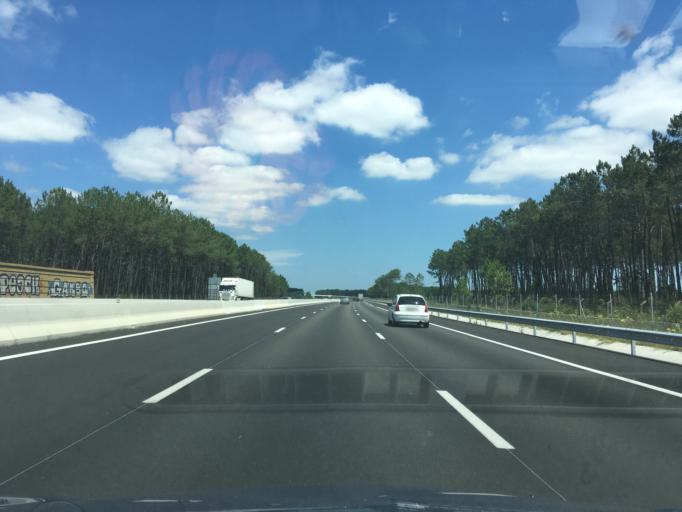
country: FR
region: Aquitaine
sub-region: Departement des Landes
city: Saint-Vincent-de-Tyrosse
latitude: 43.6805
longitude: -1.2982
